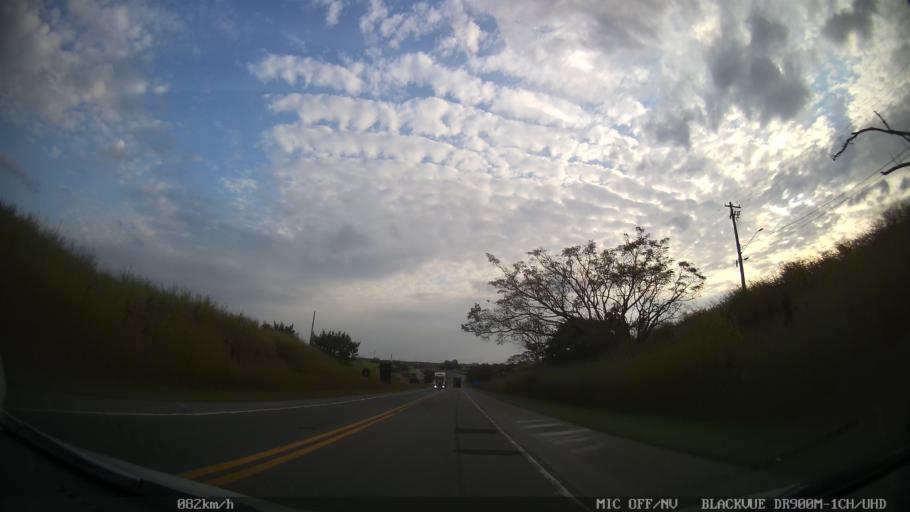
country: BR
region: Sao Paulo
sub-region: Americana
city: Americana
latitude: -22.6377
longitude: -47.3243
